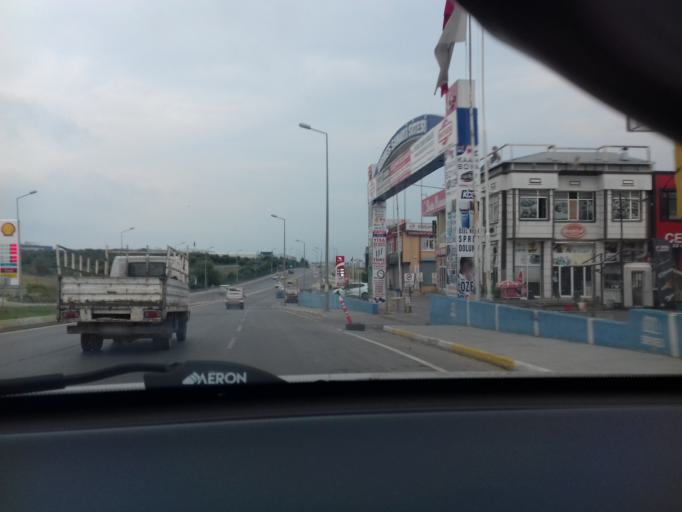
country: TR
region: Istanbul
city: Icmeler
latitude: 40.8818
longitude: 29.3466
